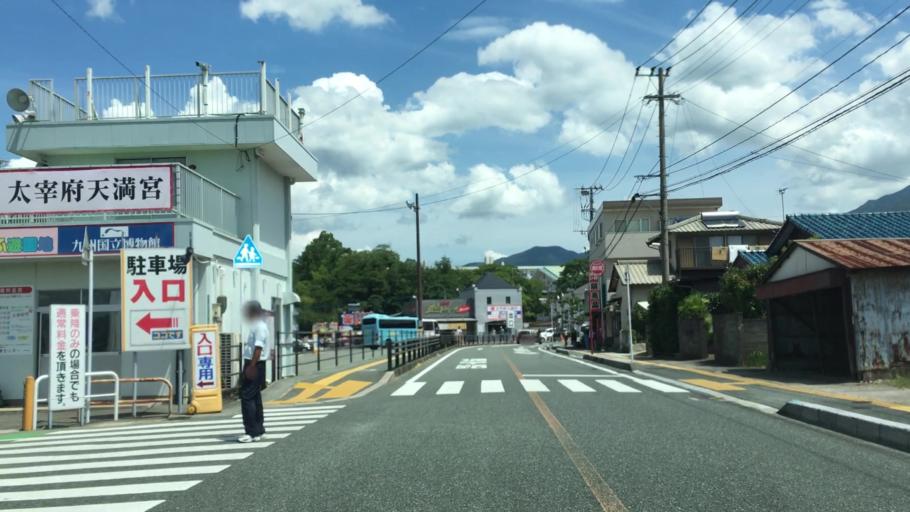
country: JP
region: Fukuoka
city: Dazaifu
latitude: 33.5187
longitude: 130.5288
